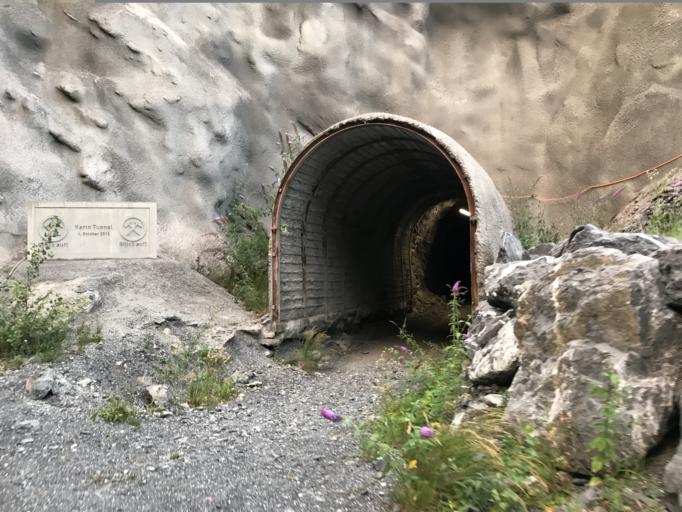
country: LI
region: Balzers
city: Balzers
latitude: 47.0685
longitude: 9.4695
